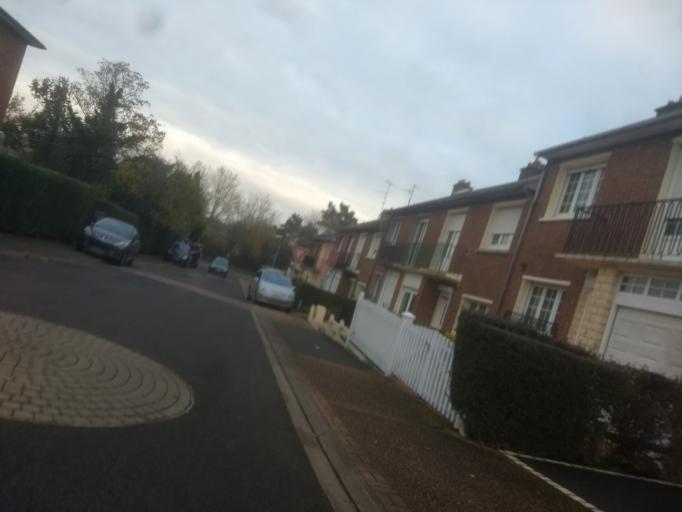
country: FR
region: Nord-Pas-de-Calais
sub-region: Departement du Pas-de-Calais
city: Anzin-Saint-Aubin
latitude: 50.2974
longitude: 2.7477
